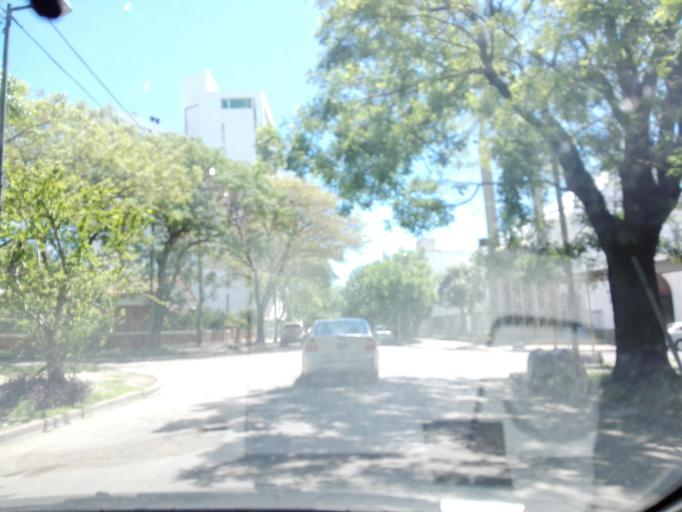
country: AR
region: Buenos Aires
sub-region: Partido de La Plata
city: La Plata
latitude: -34.9319
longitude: -57.9633
